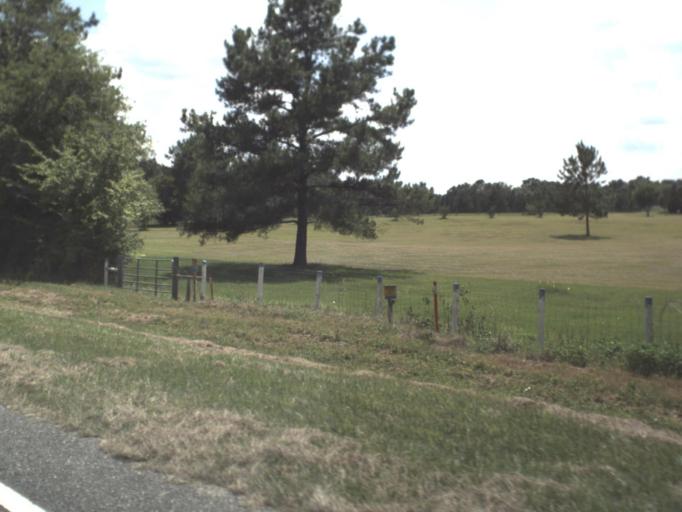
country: US
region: Florida
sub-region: Alachua County
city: High Springs
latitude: 29.9803
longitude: -82.5987
